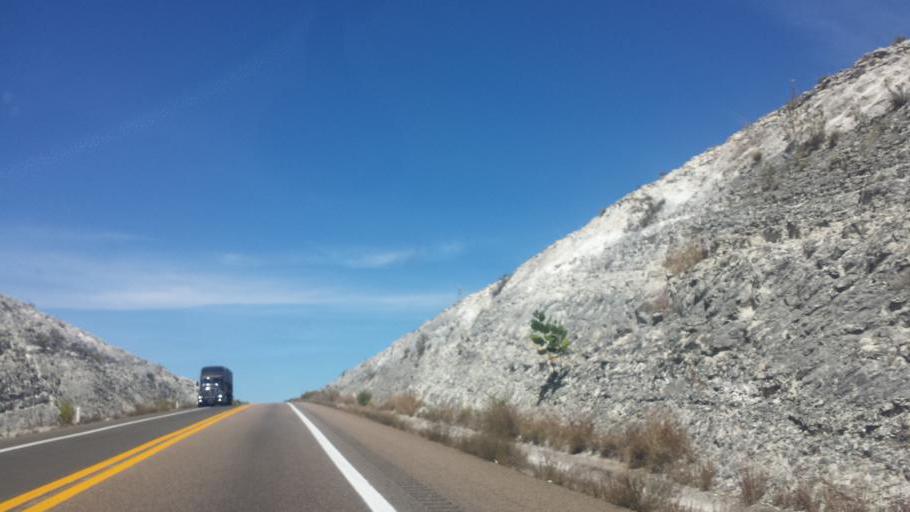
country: MX
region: Oaxaca
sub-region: Villa Tejupam de la Union
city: Villa Tejupam de la Union
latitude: 17.8311
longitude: -97.3723
